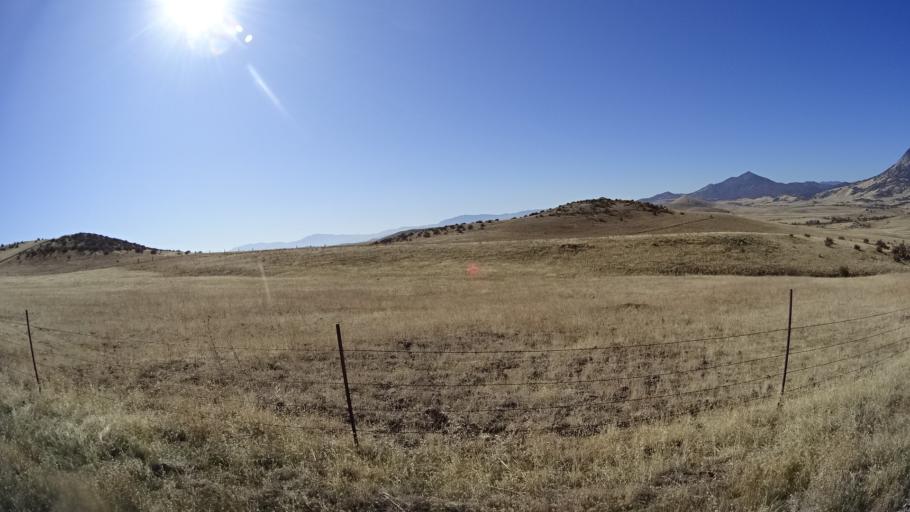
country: US
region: California
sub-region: Siskiyou County
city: Montague
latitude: 41.8455
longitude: -122.4317
